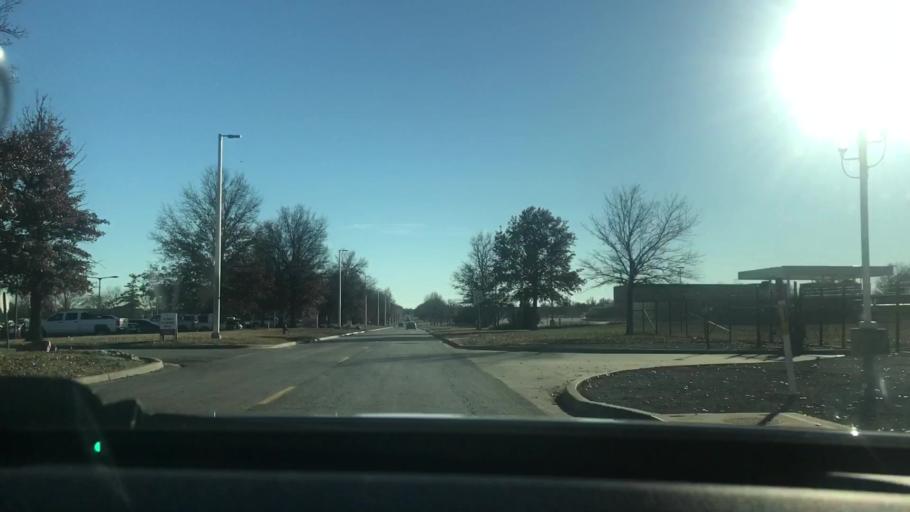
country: US
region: Missouri
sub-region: Platte County
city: Weatherby Lake
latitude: 39.3114
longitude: -94.7149
